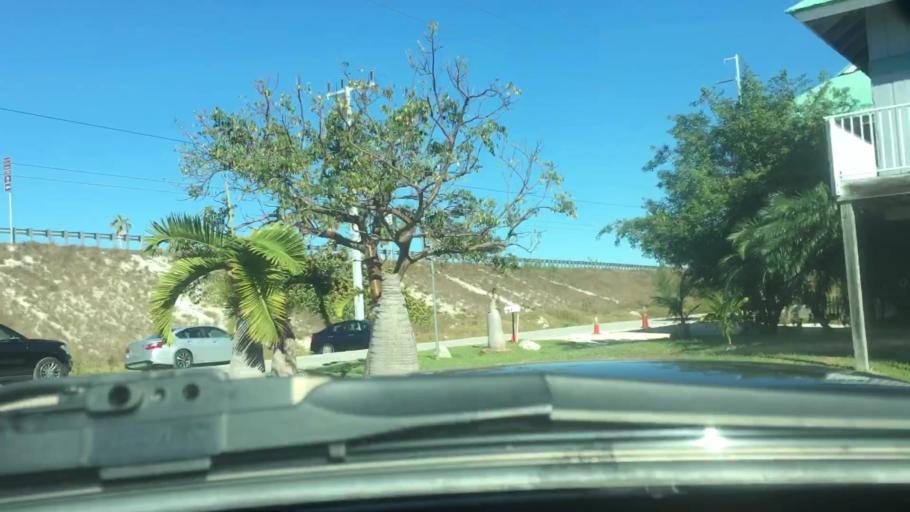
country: US
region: Florida
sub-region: Monroe County
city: Marathon
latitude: 24.7066
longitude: -81.1233
